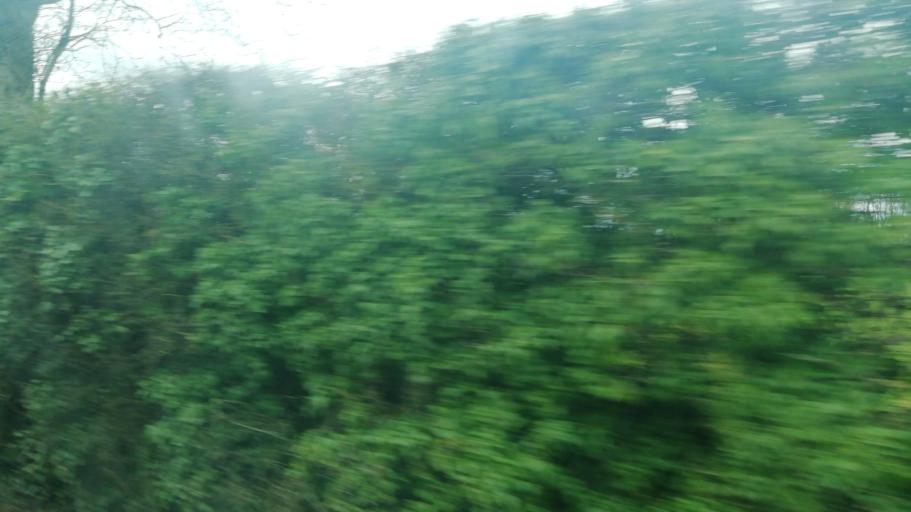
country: IE
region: Leinster
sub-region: Kildare
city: Maynooth
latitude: 53.3558
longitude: -6.6390
